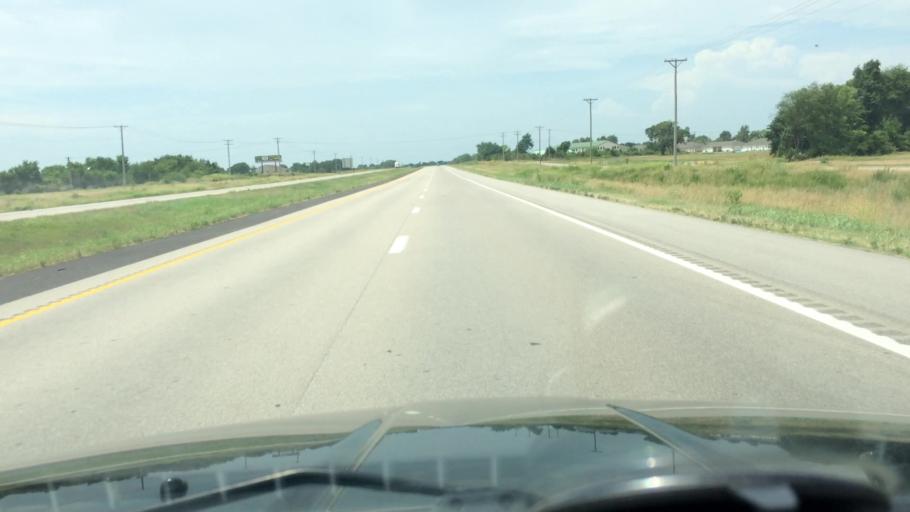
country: US
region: Missouri
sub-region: Polk County
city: Bolivar
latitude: 37.5840
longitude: -93.4145
